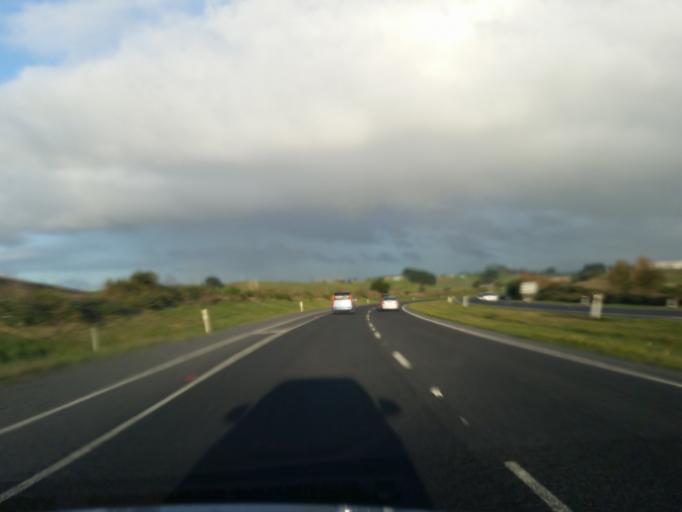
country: NZ
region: Waikato
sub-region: Waikato District
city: Te Kauwhata
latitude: -37.3481
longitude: 175.0765
